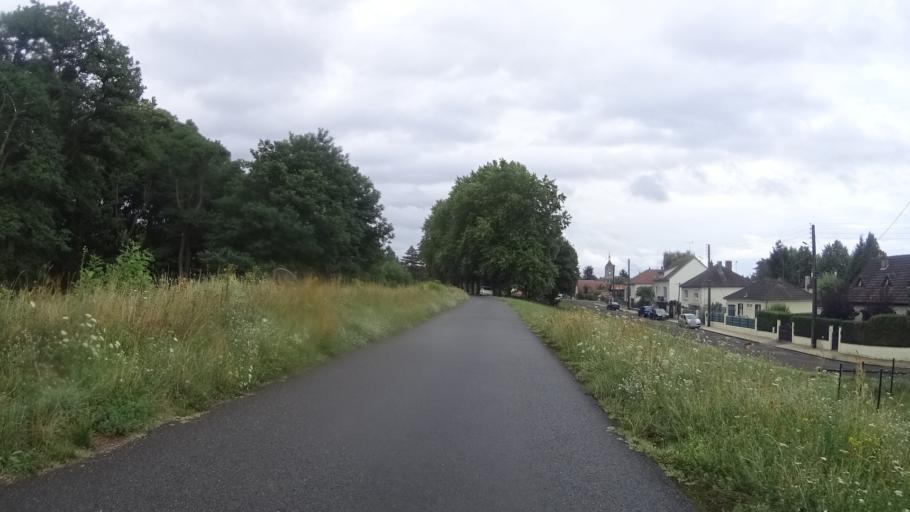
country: FR
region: Centre
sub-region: Departement du Loiret
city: Jargeau
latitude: 47.8683
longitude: 2.1134
